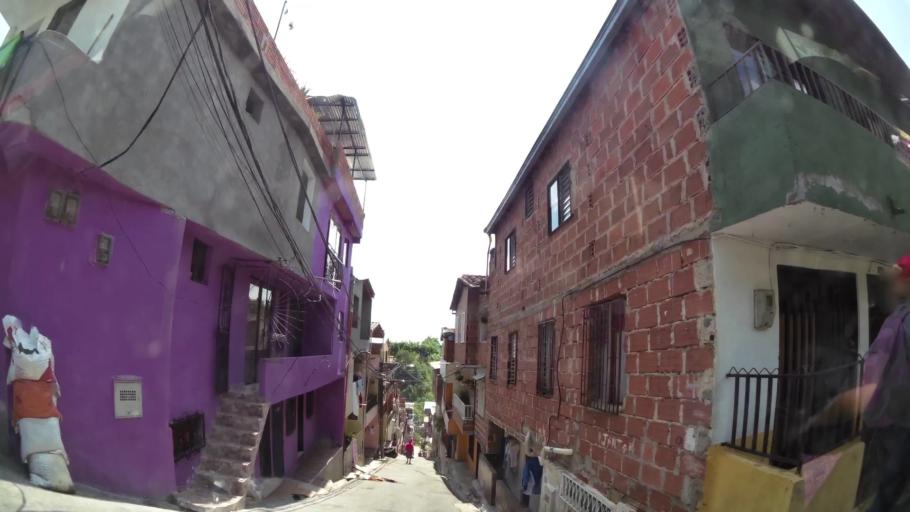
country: CO
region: Antioquia
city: La Estrella
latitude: 6.1816
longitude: -75.6584
